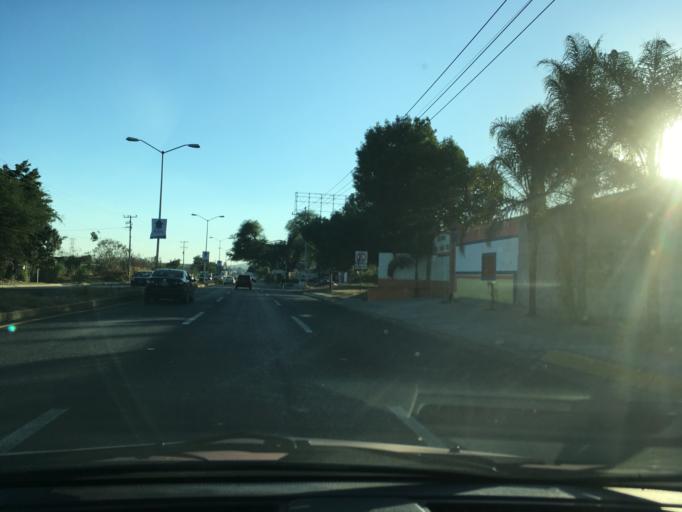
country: MX
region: Jalisco
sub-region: Tlajomulco de Zuniga
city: La Tijera
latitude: 20.5835
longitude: -103.4252
